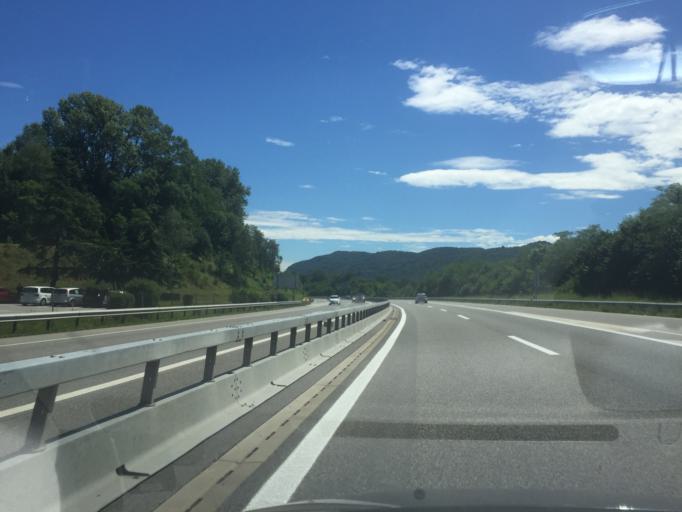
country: CH
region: Ticino
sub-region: Mendrisio District
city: Novazzano
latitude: 45.8496
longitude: 8.9848
